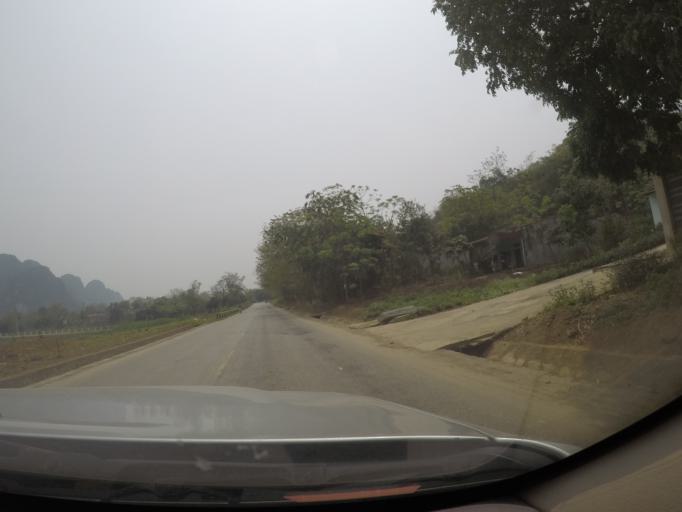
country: VN
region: Thanh Hoa
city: Thi Tran Ngoc Lac
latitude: 20.0693
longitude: 105.3842
